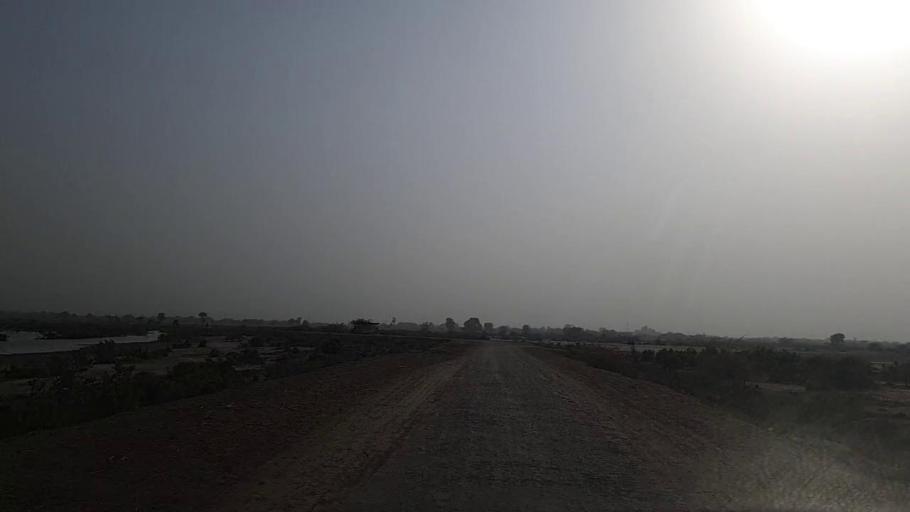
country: PK
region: Sindh
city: Pithoro
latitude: 25.4064
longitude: 69.2643
